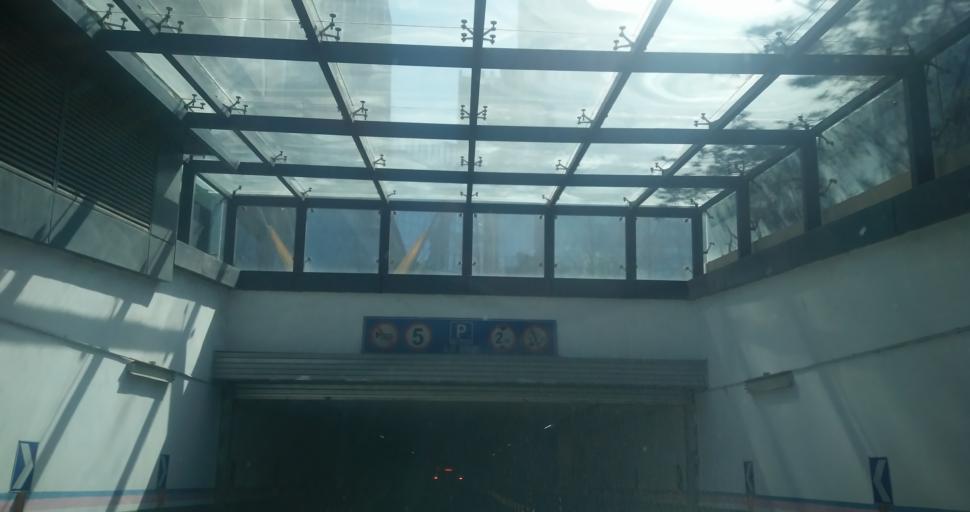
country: CN
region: Beijing
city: Jiugong
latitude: 39.8048
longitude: 116.4952
